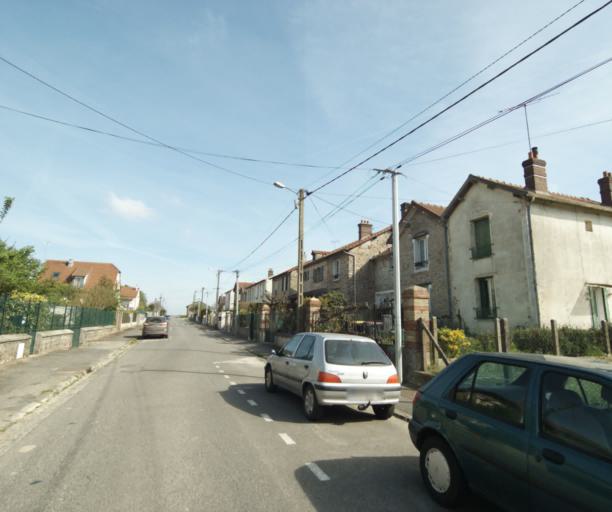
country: FR
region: Ile-de-France
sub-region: Departement de Seine-et-Marne
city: Nangis
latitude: 48.5635
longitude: 3.0131
